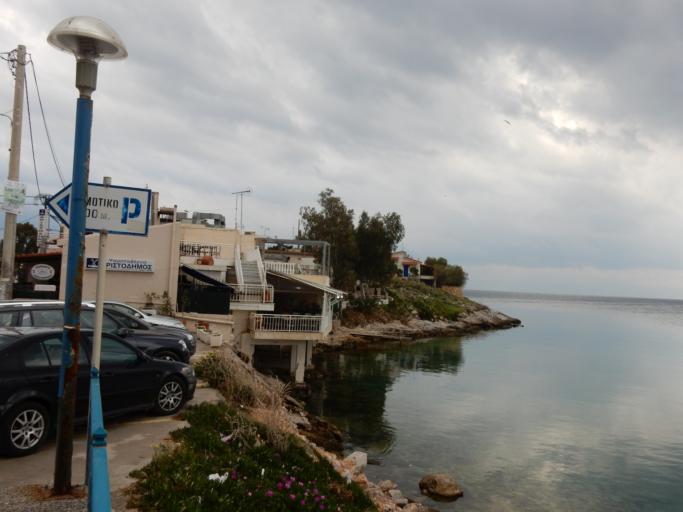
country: GR
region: Attica
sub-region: Nomarchia Dytikis Attikis
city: Megara
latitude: 37.9744
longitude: 23.3616
